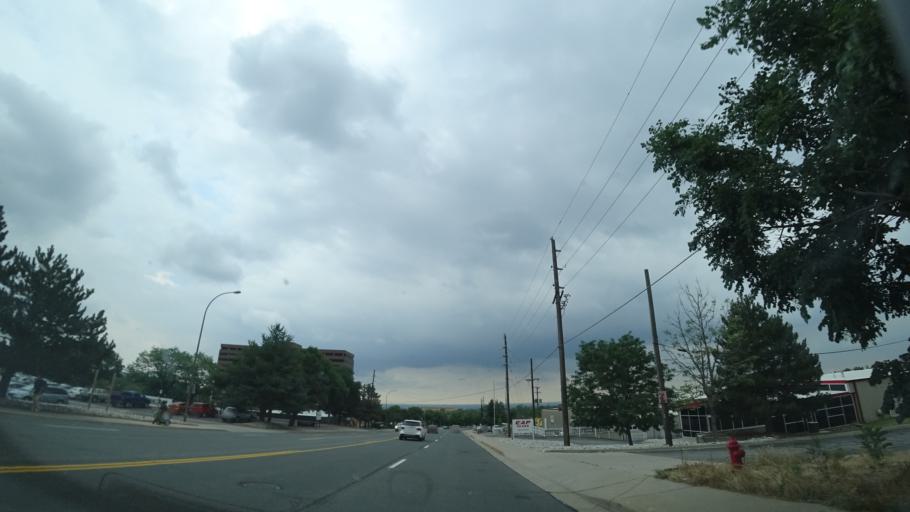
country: US
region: Colorado
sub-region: Jefferson County
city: West Pleasant View
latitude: 39.7121
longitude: -105.1374
